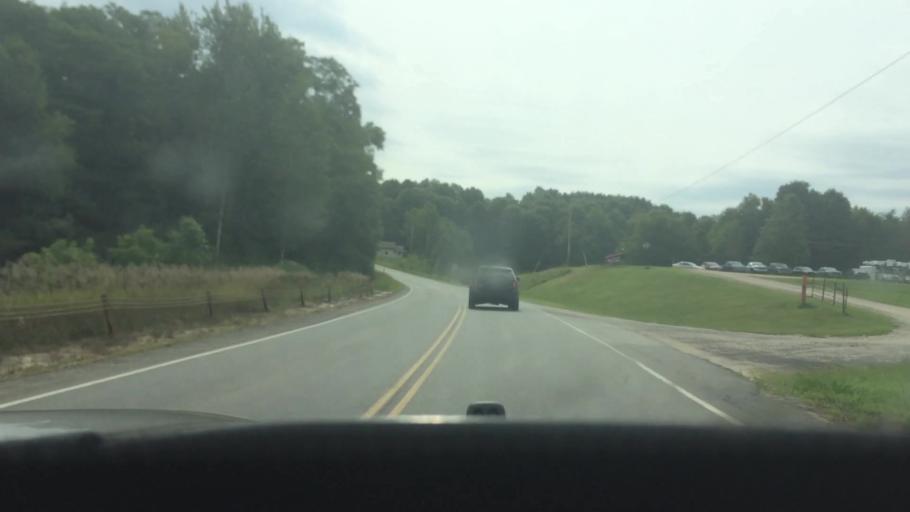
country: US
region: New York
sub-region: St. Lawrence County
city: Canton
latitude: 44.4719
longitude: -75.2378
